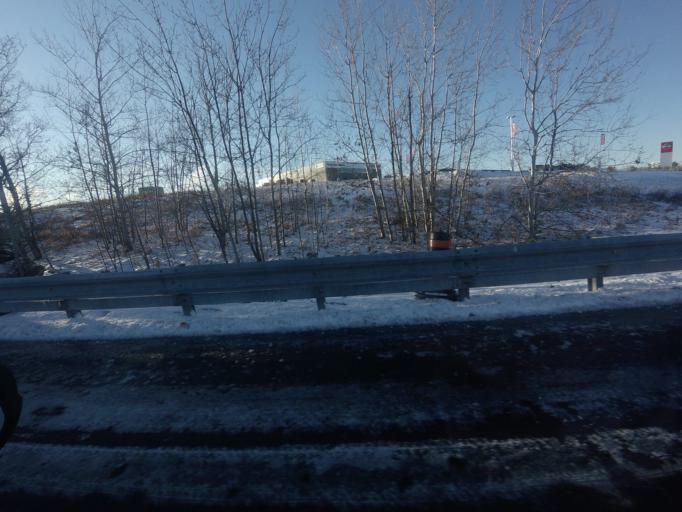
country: CA
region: Ontario
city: Bells Corners
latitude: 45.2725
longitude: -75.7986
